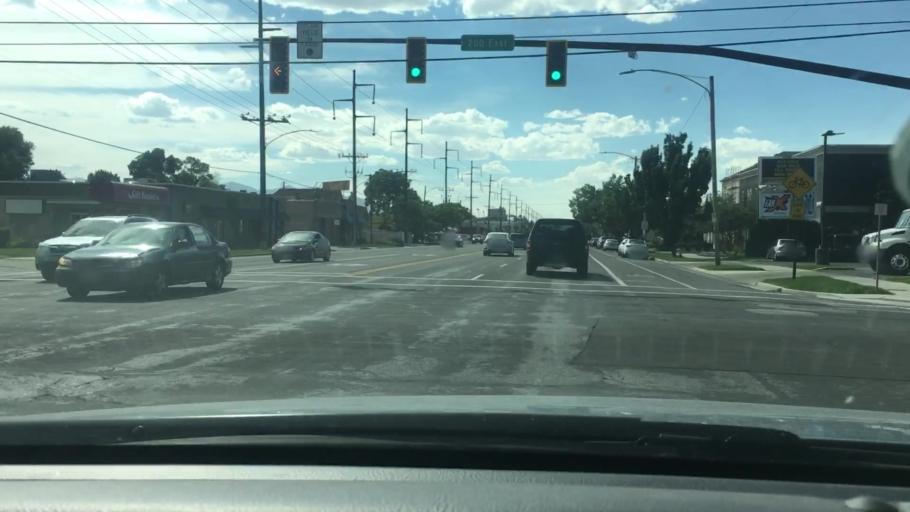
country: US
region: Utah
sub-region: Salt Lake County
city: Salt Lake City
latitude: 40.7520
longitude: -111.8853
